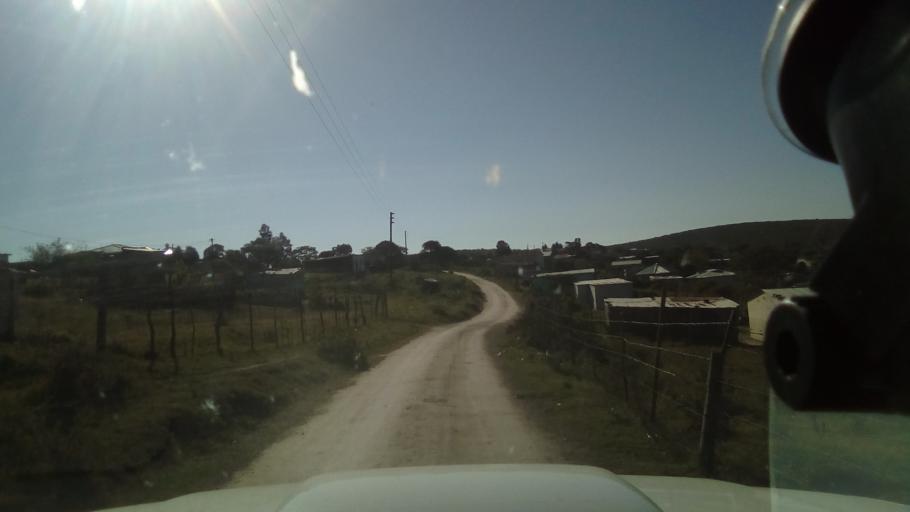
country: ZA
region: Eastern Cape
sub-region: Buffalo City Metropolitan Municipality
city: Bhisho
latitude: -32.8031
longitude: 27.3398
